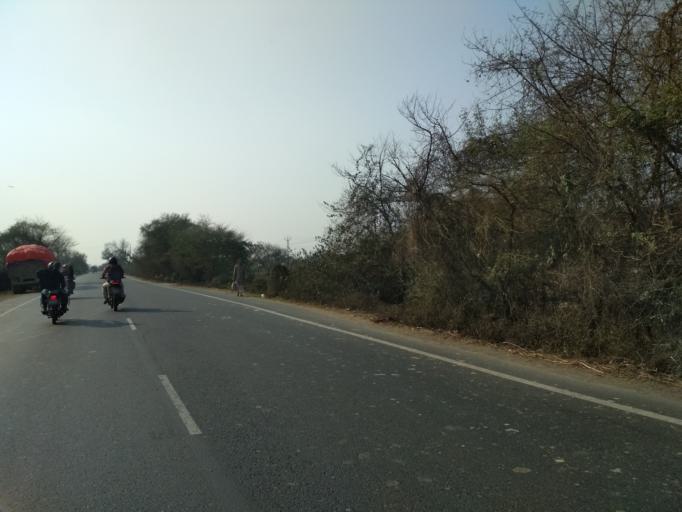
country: IN
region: Bihar
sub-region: Khagaria
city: Khagaria
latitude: 25.5076
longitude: 86.5492
